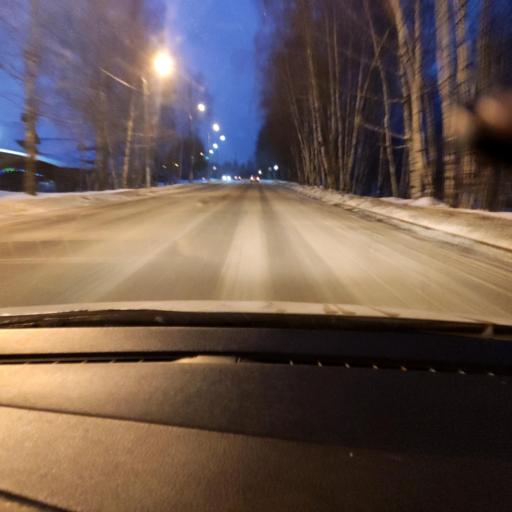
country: RU
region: Tatarstan
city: Aysha
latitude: 55.8713
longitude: 48.5778
